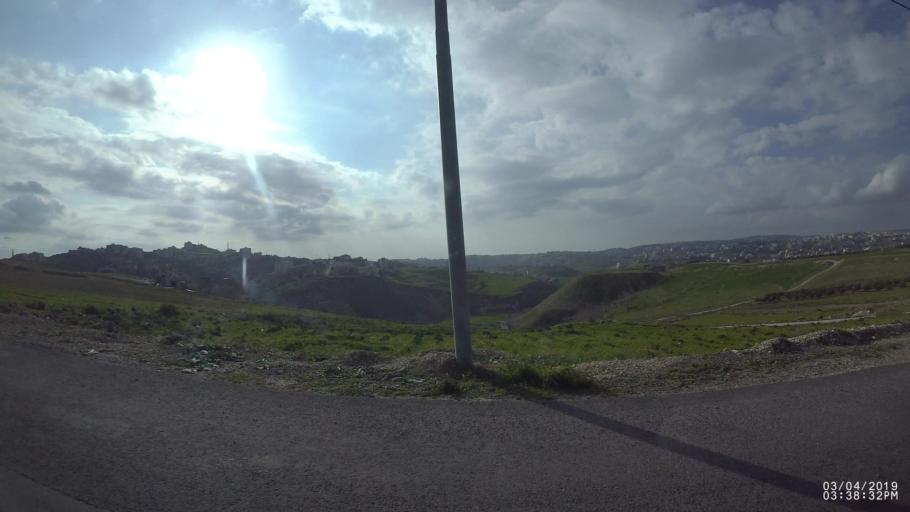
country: JO
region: Amman
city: Umm as Summaq
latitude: 31.9196
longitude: 35.8488
